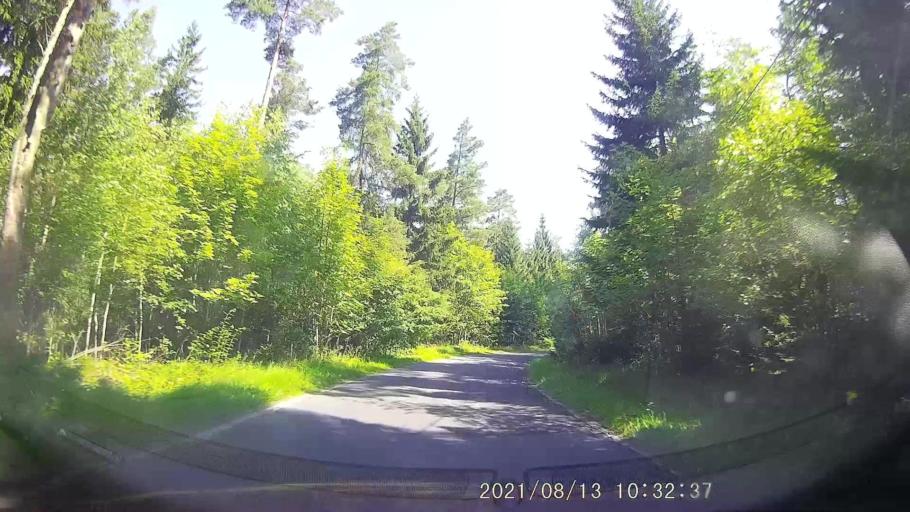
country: PL
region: Lower Silesian Voivodeship
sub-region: Powiat klodzki
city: Duszniki-Zdroj
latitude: 50.4183
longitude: 16.3829
